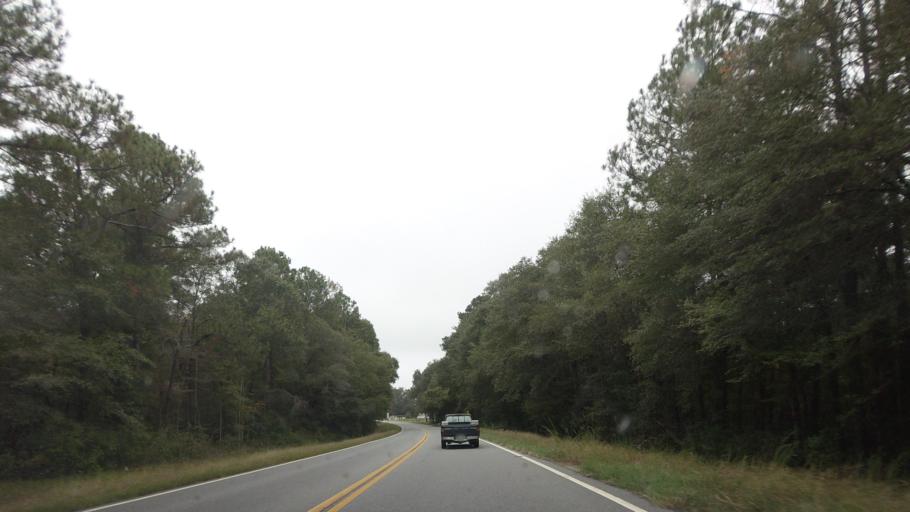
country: US
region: Georgia
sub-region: Berrien County
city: Enigma
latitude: 31.4191
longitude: -83.2439
